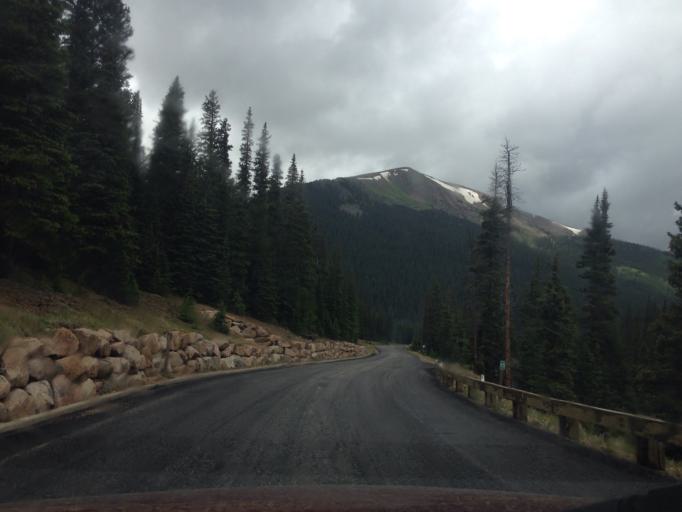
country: US
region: Colorado
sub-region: Clear Creek County
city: Georgetown
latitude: 39.6056
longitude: -105.7120
